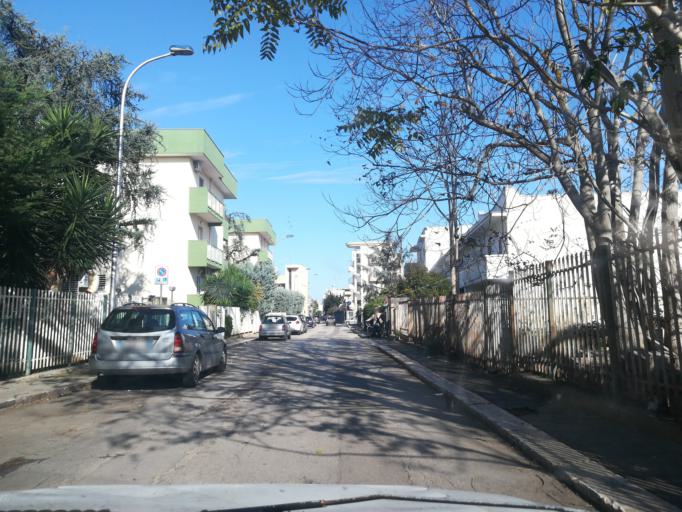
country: IT
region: Apulia
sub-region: Provincia di Bari
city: Modugno
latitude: 41.0769
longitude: 16.7832
